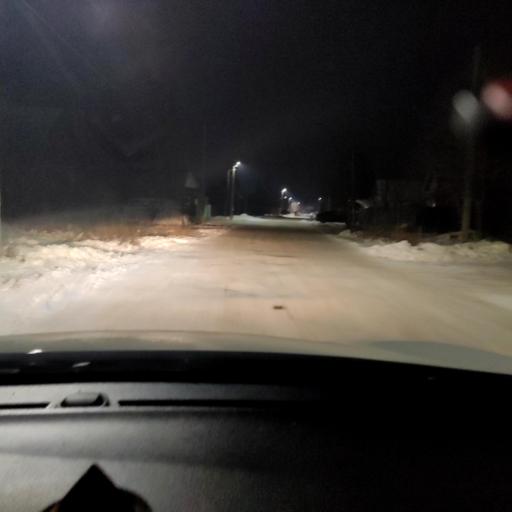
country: RU
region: Tatarstan
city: Stolbishchi
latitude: 55.6527
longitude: 49.2091
